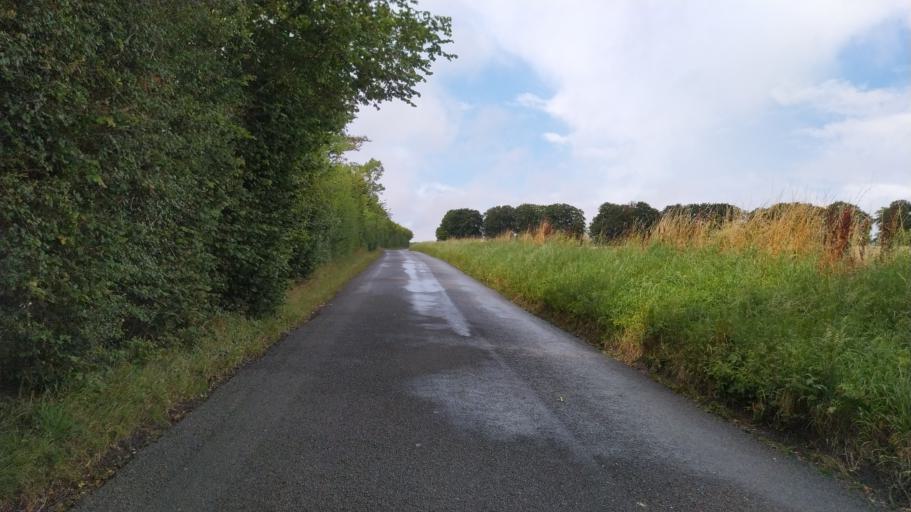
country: GB
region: England
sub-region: Hampshire
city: Swanmore
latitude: 51.0106
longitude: -1.1430
